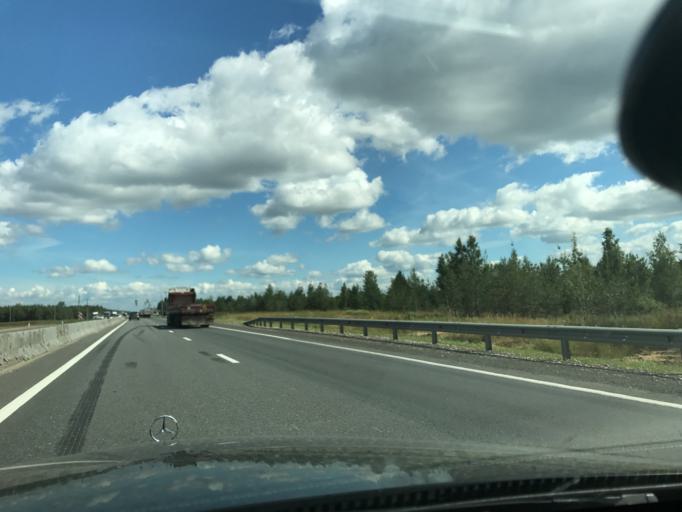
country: RU
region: Nizjnij Novgorod
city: Dzerzhinsk
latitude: 56.2969
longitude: 43.4396
